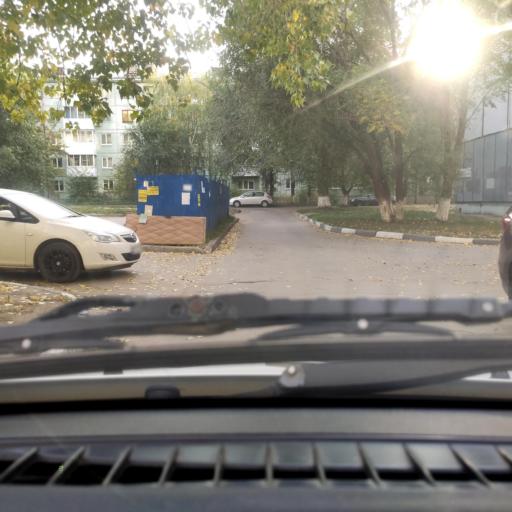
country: RU
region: Samara
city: Zhigulevsk
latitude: 53.4865
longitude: 49.4694
